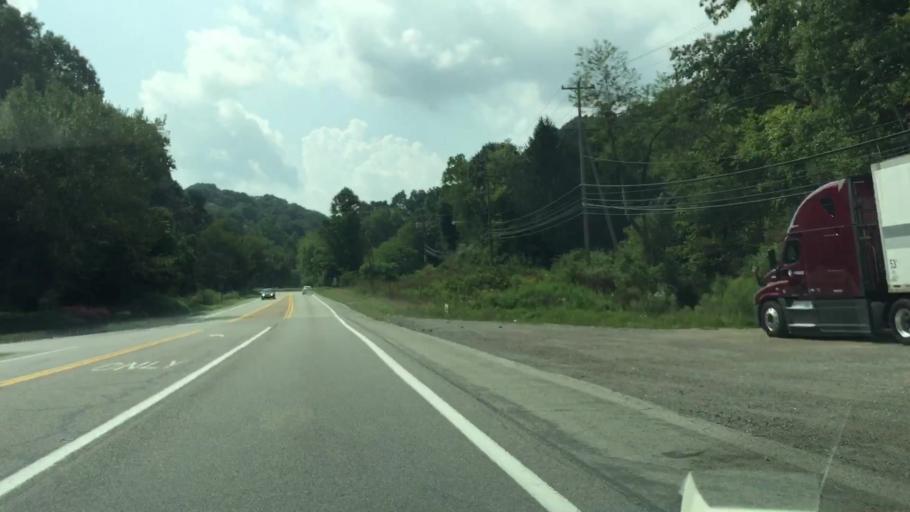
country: US
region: Pennsylvania
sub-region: Allegheny County
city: Coraopolis
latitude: 40.4638
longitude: -80.1522
